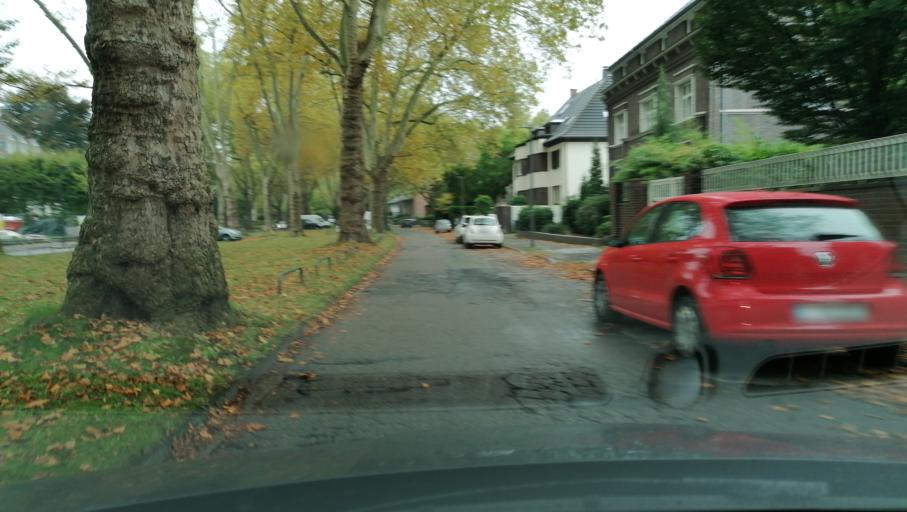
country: DE
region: North Rhine-Westphalia
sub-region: Regierungsbezirk Munster
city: Gelsenkirchen
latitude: 51.5066
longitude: 7.0838
